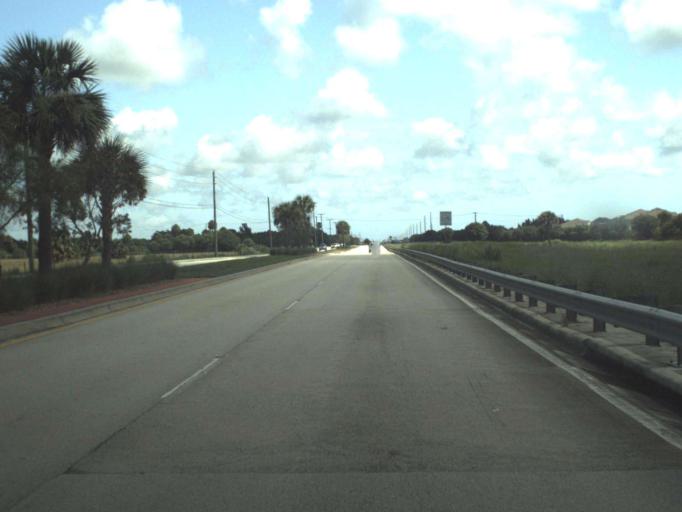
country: US
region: Florida
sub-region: Indian River County
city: Vero Beach South
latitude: 27.5906
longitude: -80.4473
